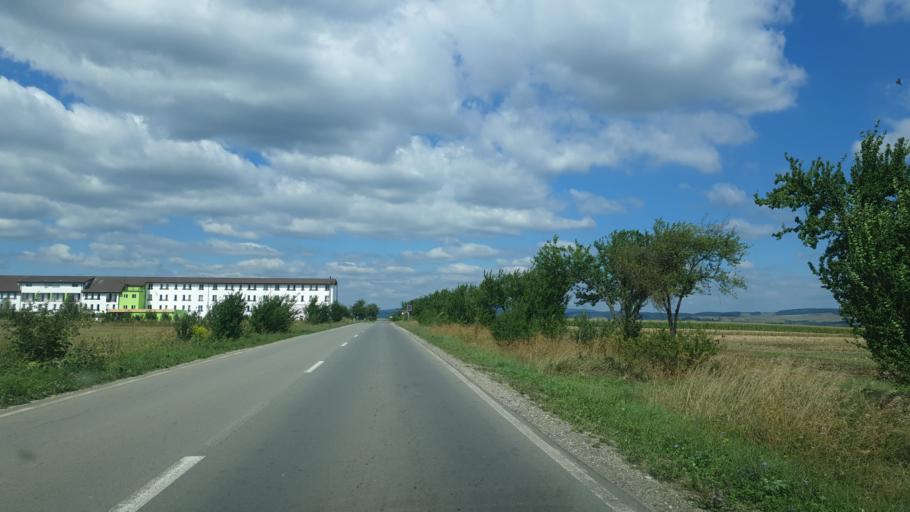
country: RO
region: Brasov
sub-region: Comuna Sanpetru
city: Sanpetru
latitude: 45.7270
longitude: 25.6281
